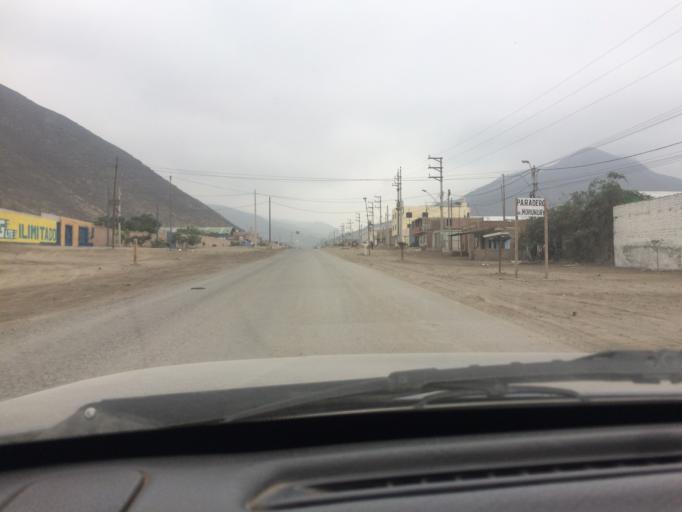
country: PE
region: Lima
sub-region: Lima
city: Cieneguilla
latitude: -12.1684
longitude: -76.8645
